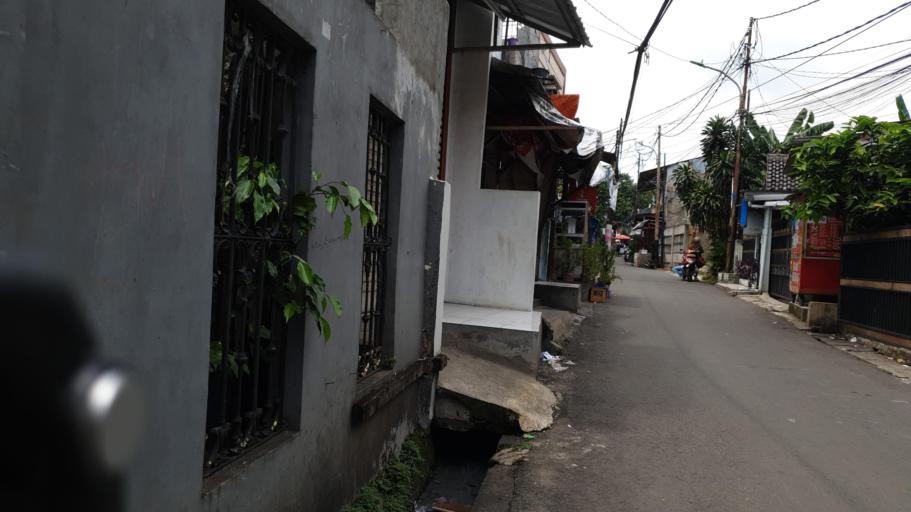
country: ID
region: Banten
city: South Tangerang
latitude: -6.2795
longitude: 106.7937
